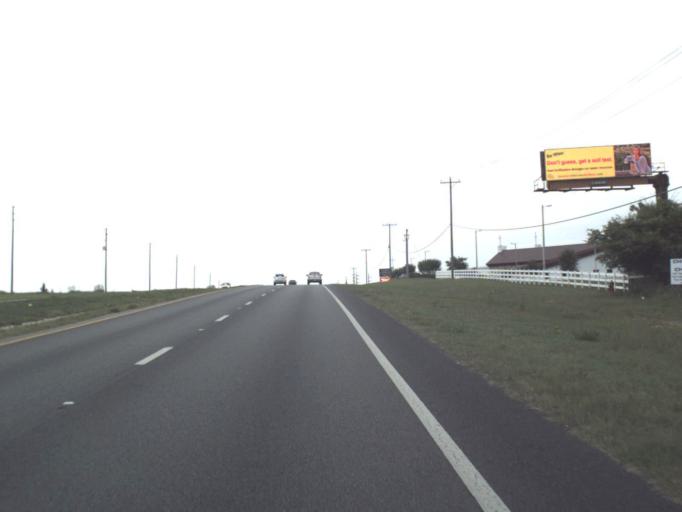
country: US
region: Florida
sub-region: Sumter County
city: The Villages
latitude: 28.9738
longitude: -81.9794
